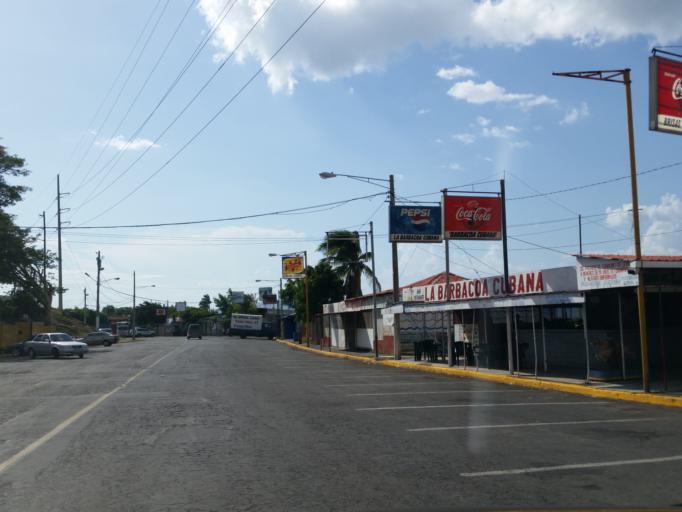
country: NI
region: Managua
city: Managua
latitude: 12.1604
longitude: -86.2729
